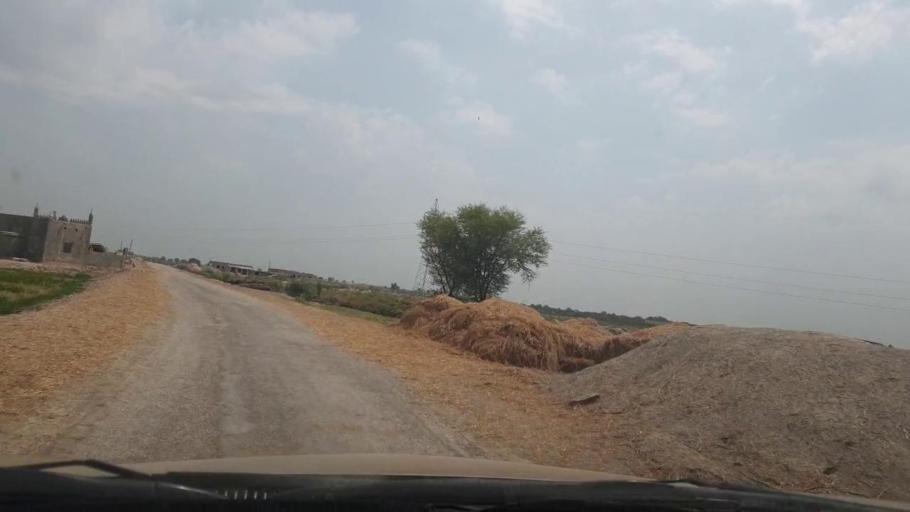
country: PK
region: Sindh
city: Ratodero
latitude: 27.7050
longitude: 68.2685
